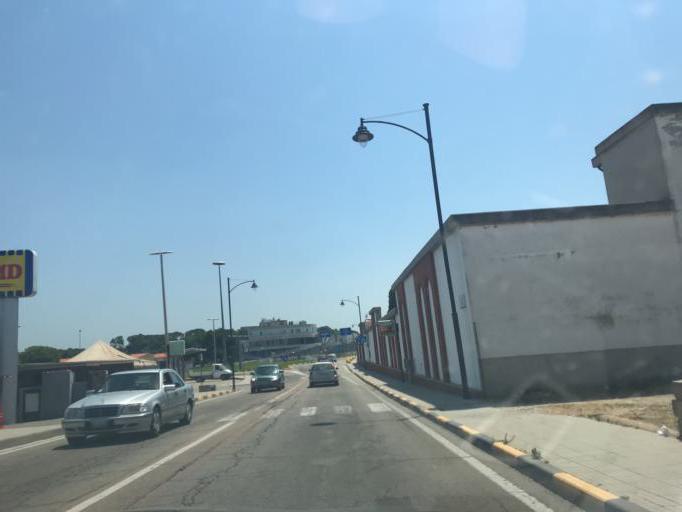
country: IT
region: Sardinia
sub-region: Provincia di Olbia-Tempio
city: Olbia
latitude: 40.9134
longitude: 9.5006
